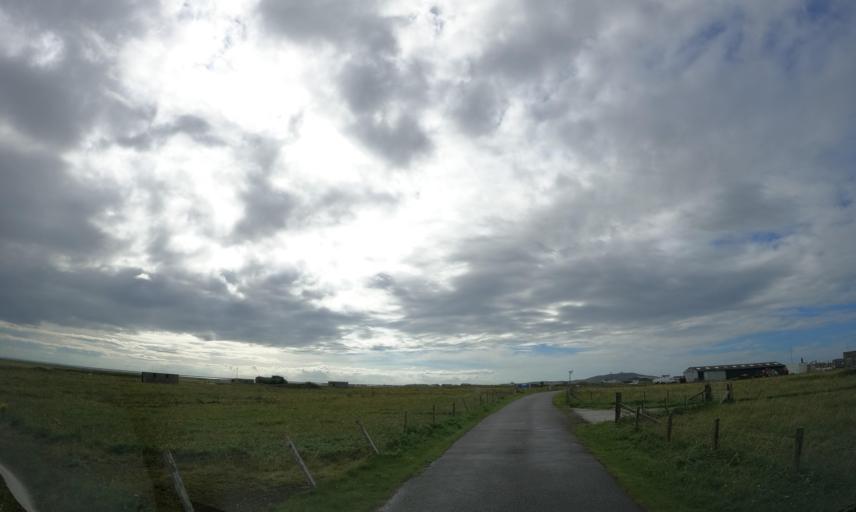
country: GB
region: Scotland
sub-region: Eilean Siar
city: Barra
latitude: 56.4978
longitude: -6.8805
